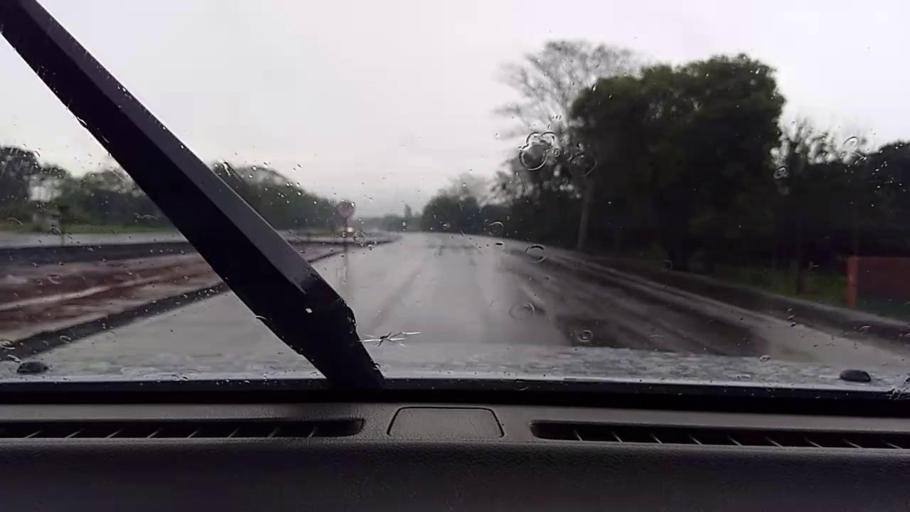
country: PY
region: Caaguazu
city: Repatriacion
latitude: -25.4540
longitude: -55.9095
